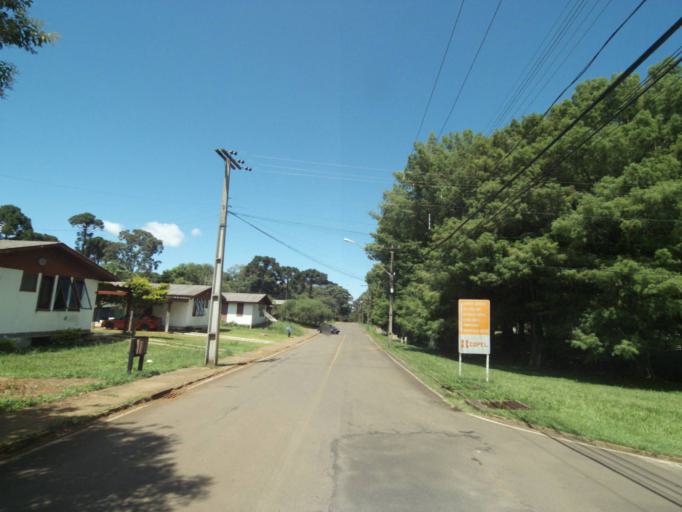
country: BR
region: Parana
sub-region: Chopinzinho
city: Chopinzinho
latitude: -25.7935
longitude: -52.0923
